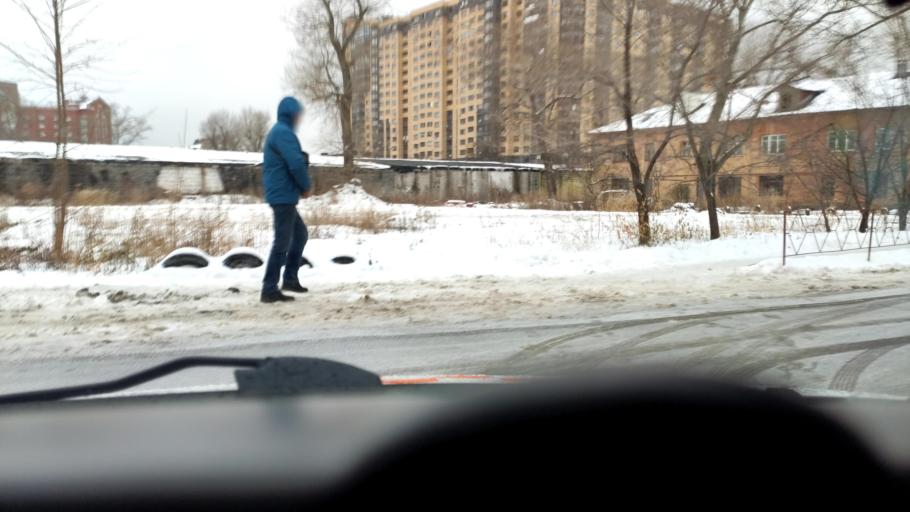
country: RU
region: Voronezj
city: Voronezh
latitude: 51.6736
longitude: 39.1680
